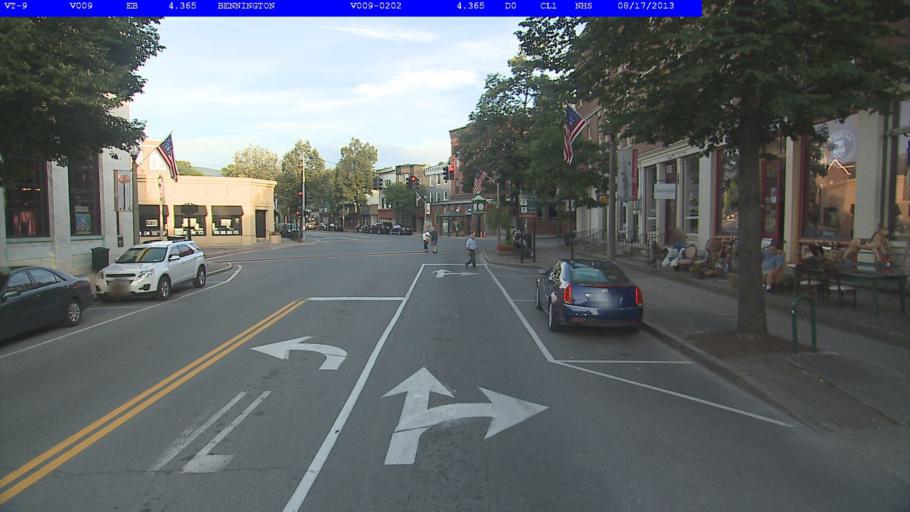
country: US
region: Vermont
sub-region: Bennington County
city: Bennington
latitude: 42.8786
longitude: -73.1976
